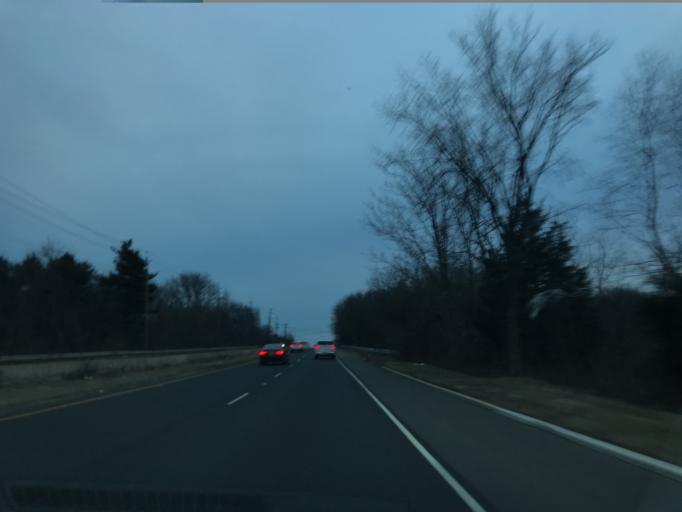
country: US
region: New Jersey
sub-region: Middlesex County
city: Dayton
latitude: 40.3685
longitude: -74.4995
